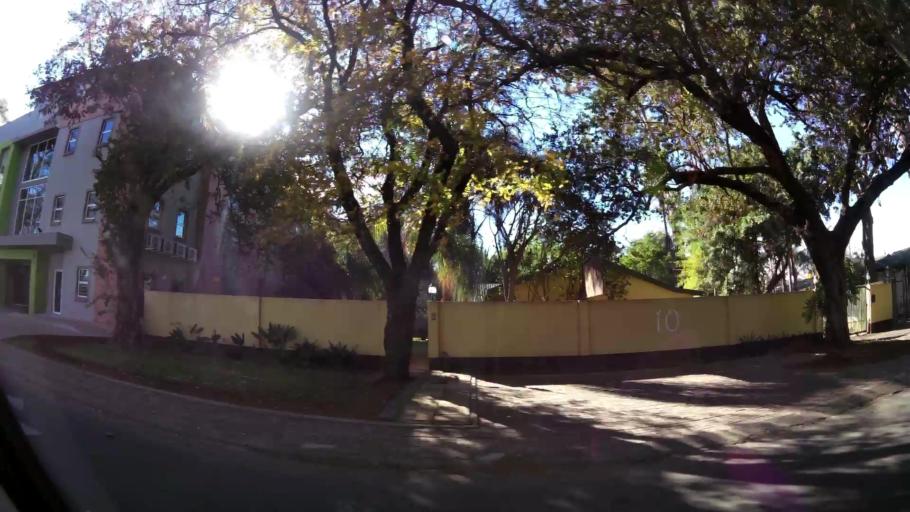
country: ZA
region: Limpopo
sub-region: Capricorn District Municipality
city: Polokwane
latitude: -23.9179
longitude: 29.4584
